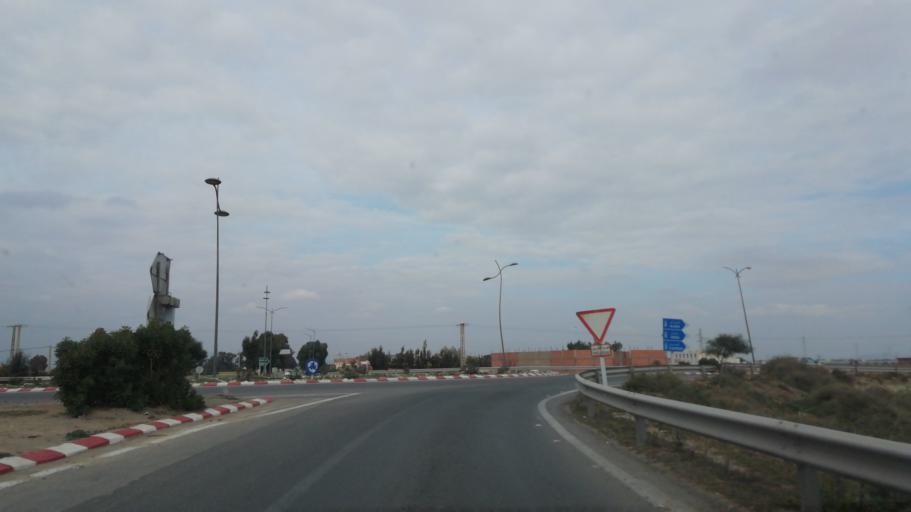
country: DZ
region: Mascara
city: Mascara
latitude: 35.6282
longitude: 0.0615
